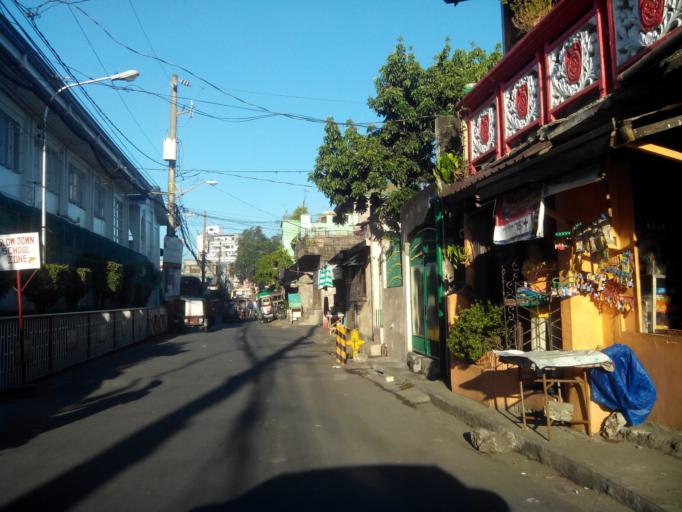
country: PH
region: Calabarzon
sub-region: Province of Rizal
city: Taytay
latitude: 14.5692
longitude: 121.1345
